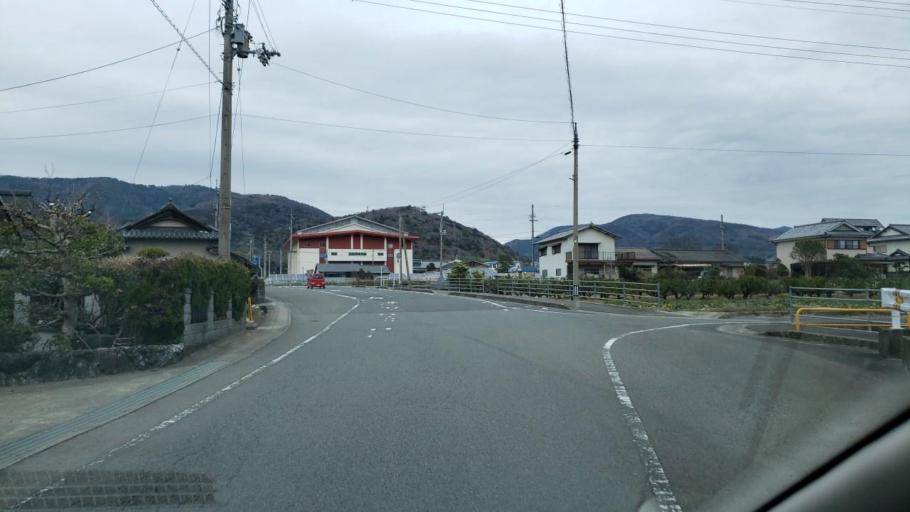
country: JP
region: Tokushima
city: Kamojimacho-jogejima
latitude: 34.1129
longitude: 134.3404
